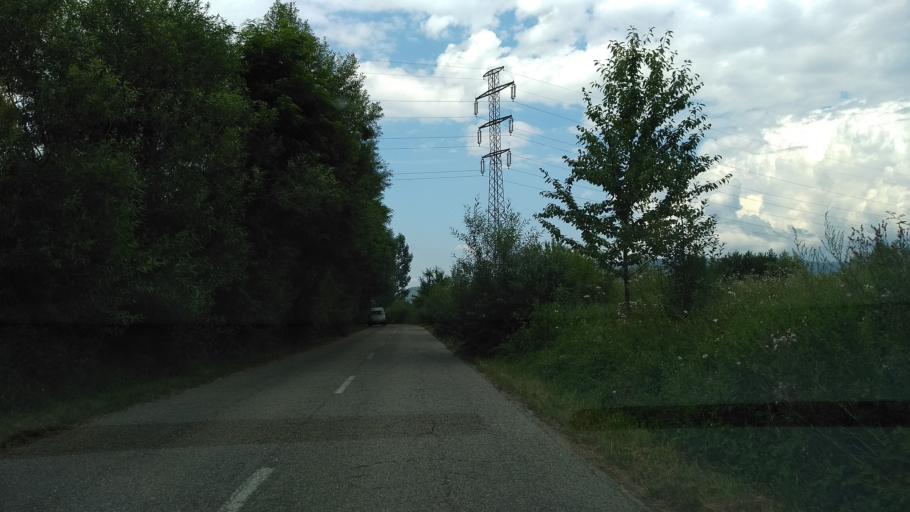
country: RO
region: Hunedoara
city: Salasu de Sus
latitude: 45.5017
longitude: 22.9492
